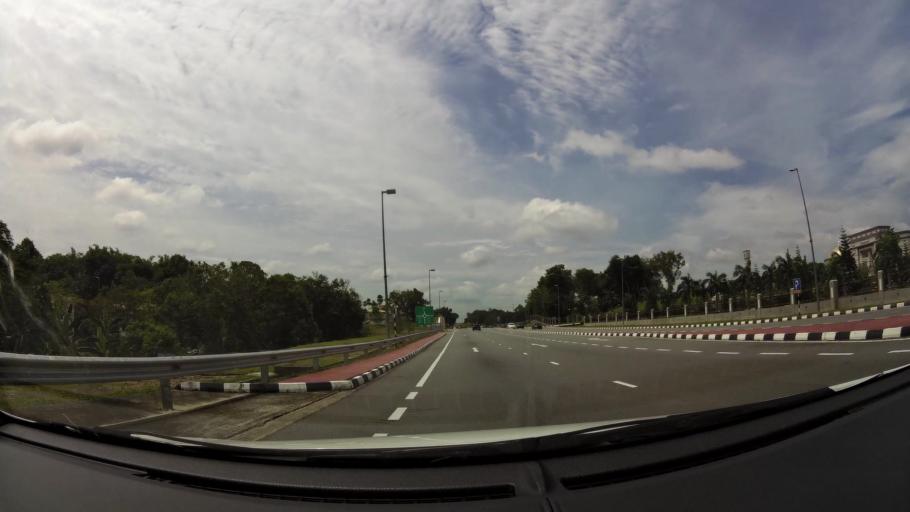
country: BN
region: Brunei and Muara
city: Bandar Seri Begawan
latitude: 4.9201
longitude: 114.9349
